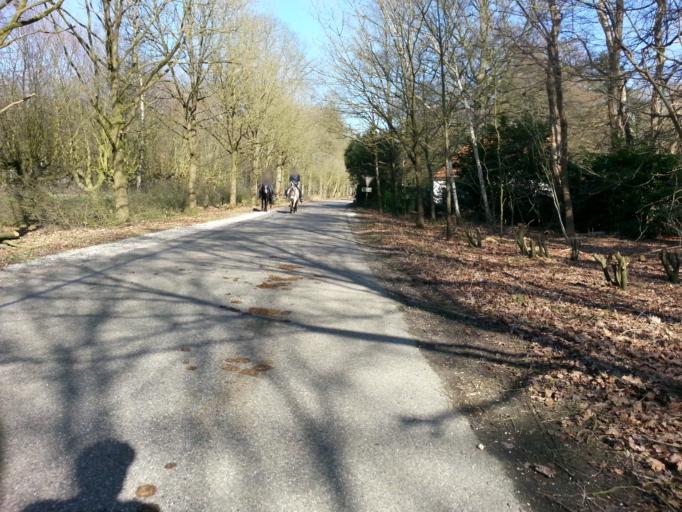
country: NL
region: Utrecht
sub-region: Gemeente Utrechtse Heuvelrug
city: Maarsbergen
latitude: 52.0226
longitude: 5.3896
